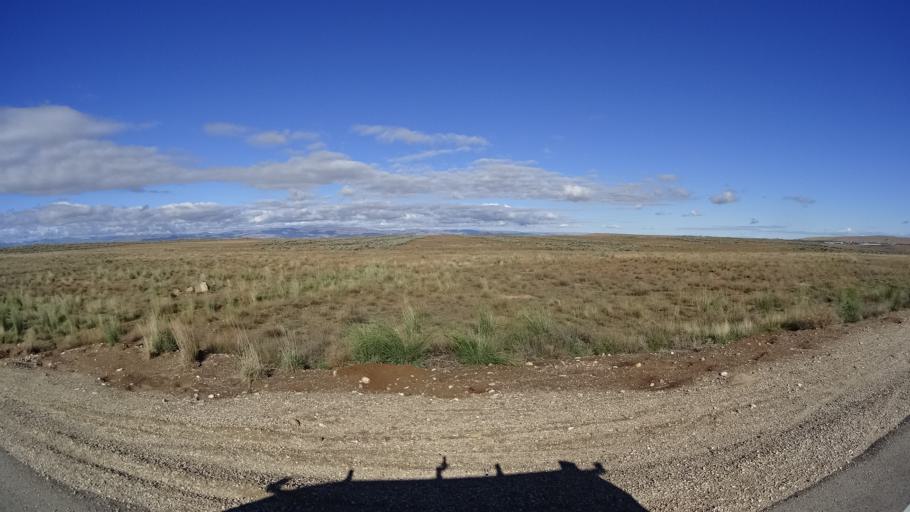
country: US
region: Idaho
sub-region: Ada County
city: Kuna
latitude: 43.3899
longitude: -116.4139
